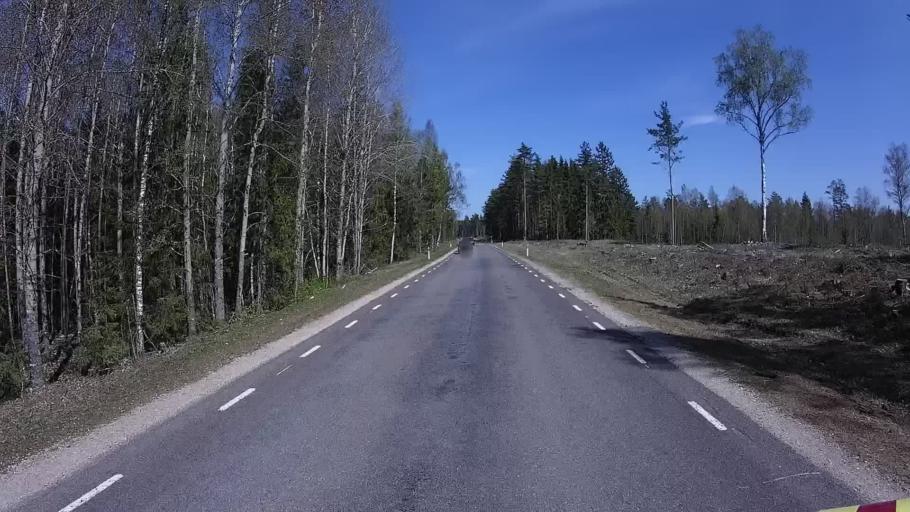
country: EE
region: Harju
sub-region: Nissi vald
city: Turba
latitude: 59.1149
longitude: 24.0541
